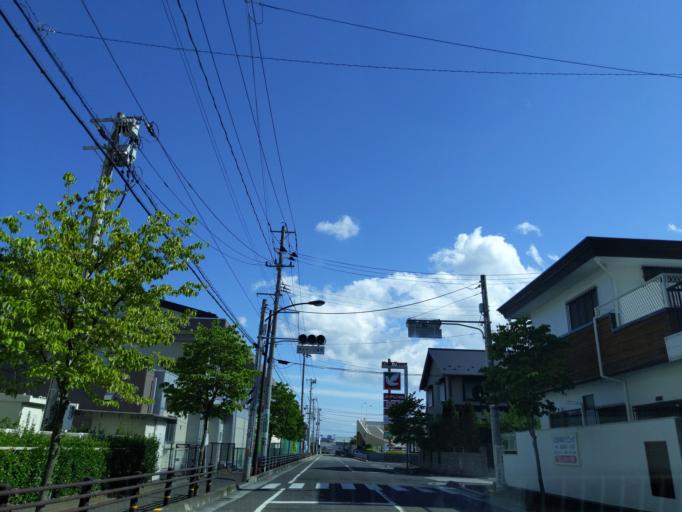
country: JP
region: Fukushima
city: Koriyama
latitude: 37.3920
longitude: 140.3789
